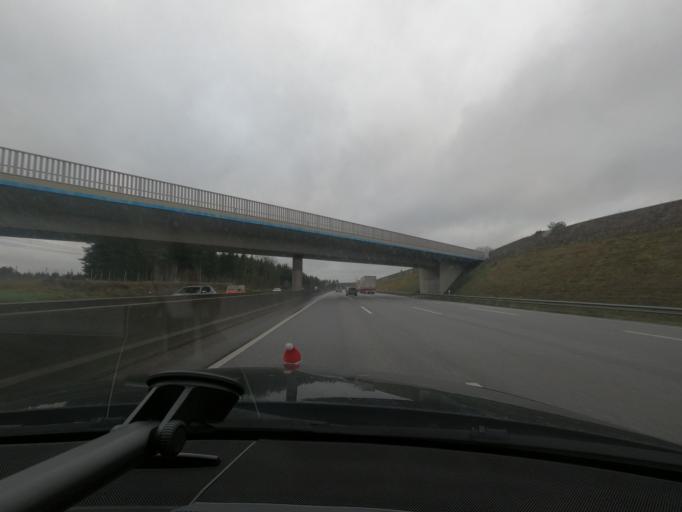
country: DE
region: Schleswig-Holstein
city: Kaltenkirchen
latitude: 53.8255
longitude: 9.9233
